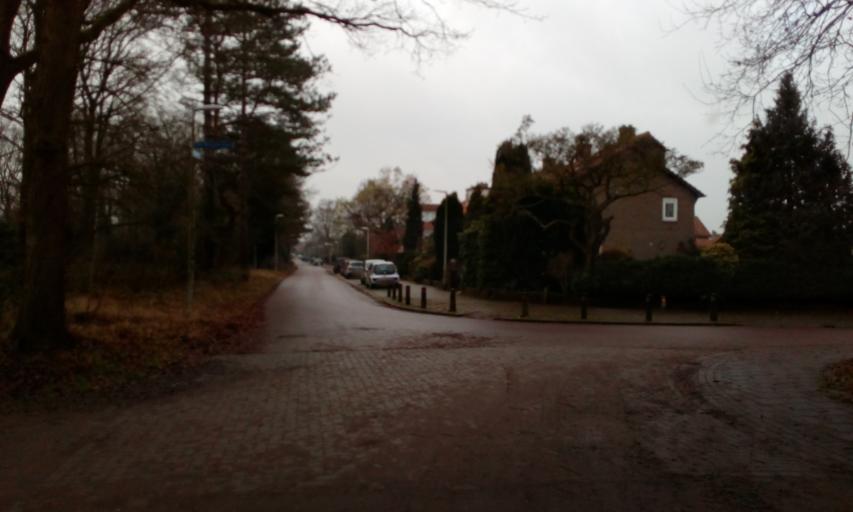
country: NL
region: North Holland
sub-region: Gemeente Bussum
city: Bussum
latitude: 52.2648
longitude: 5.1812
